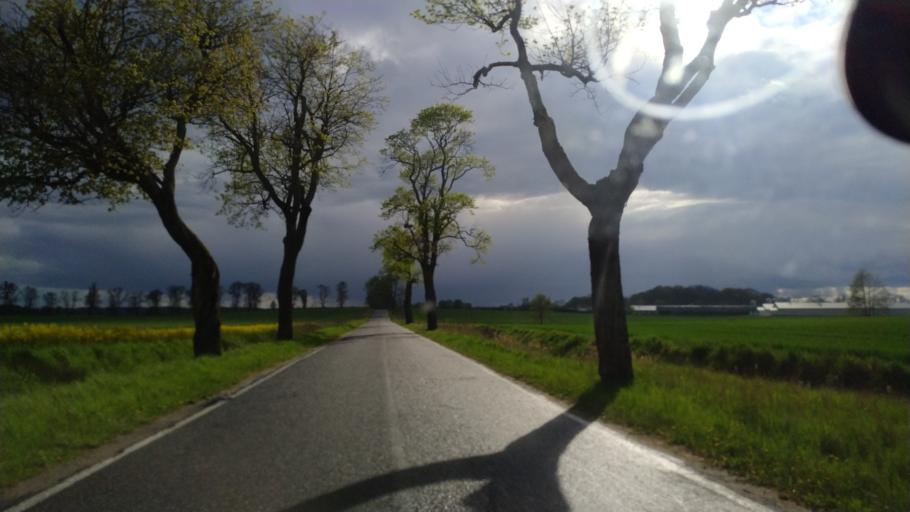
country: PL
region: Pomeranian Voivodeship
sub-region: Powiat starogardzki
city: Smetowo Graniczne
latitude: 53.7225
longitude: 18.6218
